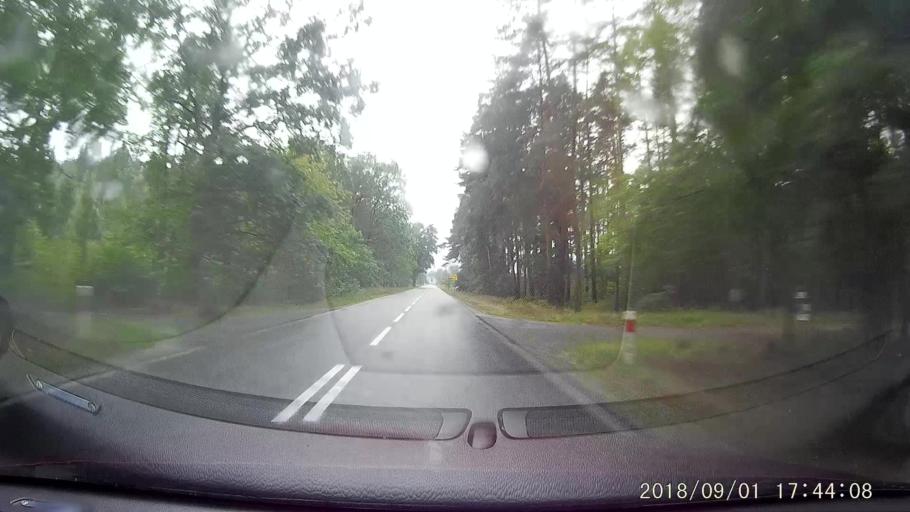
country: PL
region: Lubusz
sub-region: Powiat zaganski
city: Ilowa
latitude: 51.5361
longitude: 15.2431
